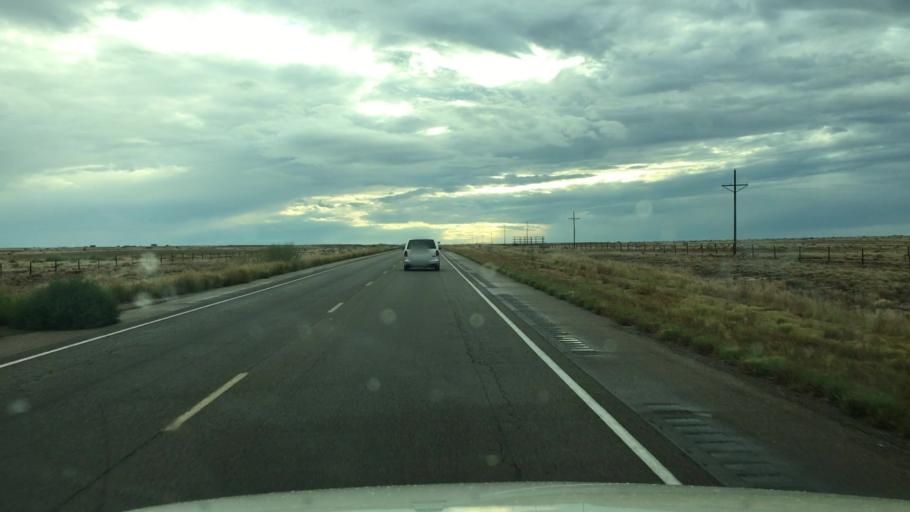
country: US
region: New Mexico
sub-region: Chaves County
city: Roswell
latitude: 33.4035
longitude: -104.3213
